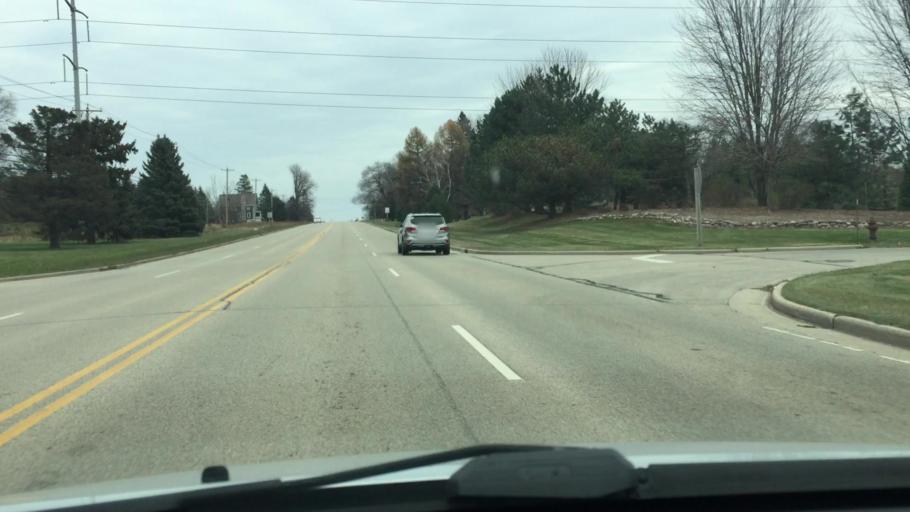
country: US
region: Wisconsin
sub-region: Ozaukee County
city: Mequon
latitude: 43.2216
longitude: -88.0150
